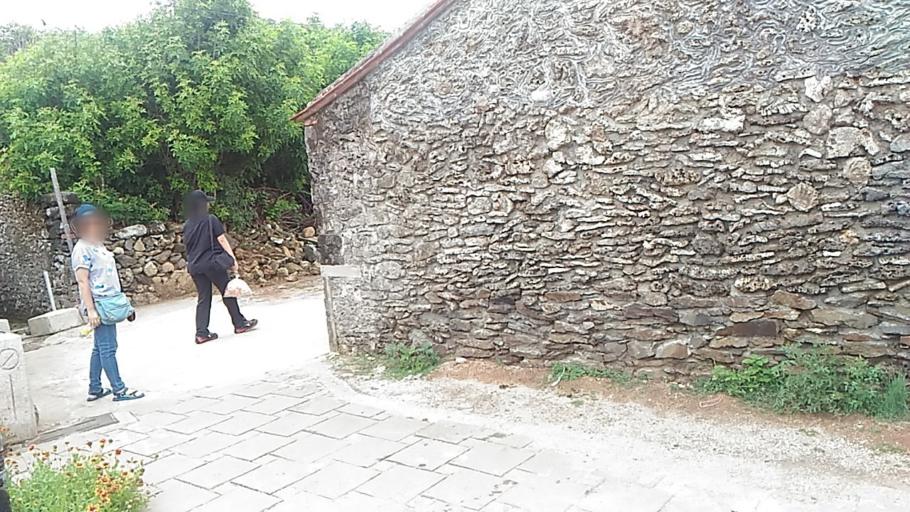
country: TW
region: Taiwan
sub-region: Penghu
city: Ma-kung
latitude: 23.3712
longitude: 119.4953
